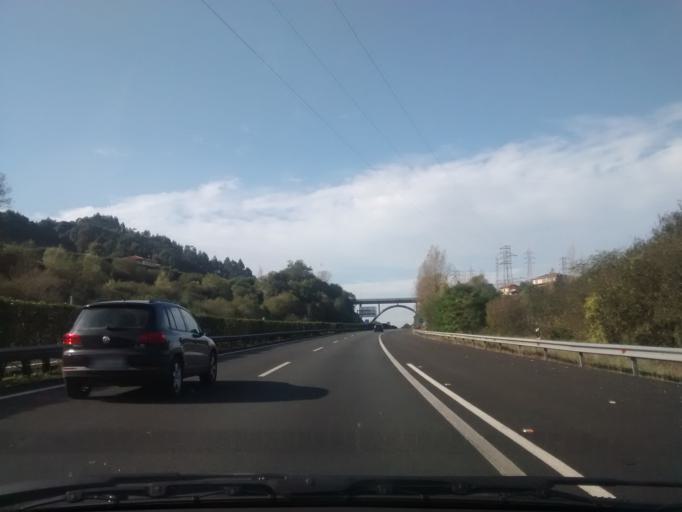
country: ES
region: Cantabria
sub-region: Provincia de Cantabria
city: Entrambasaguas
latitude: 43.3905
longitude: -3.7139
